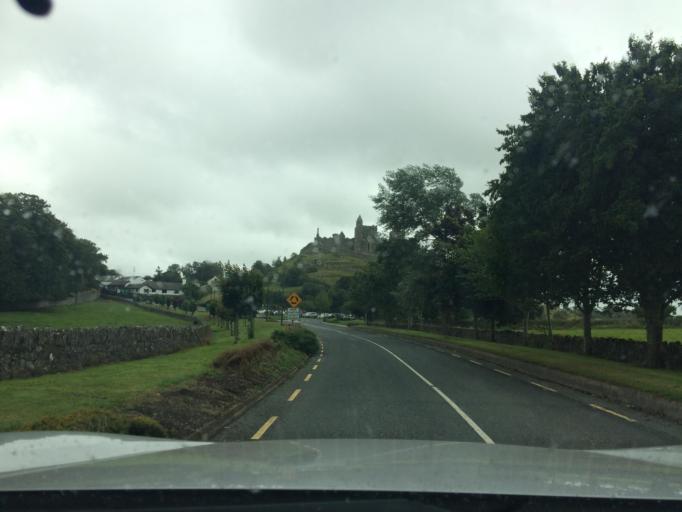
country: IE
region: Munster
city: Cashel
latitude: 52.5236
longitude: -7.8889
